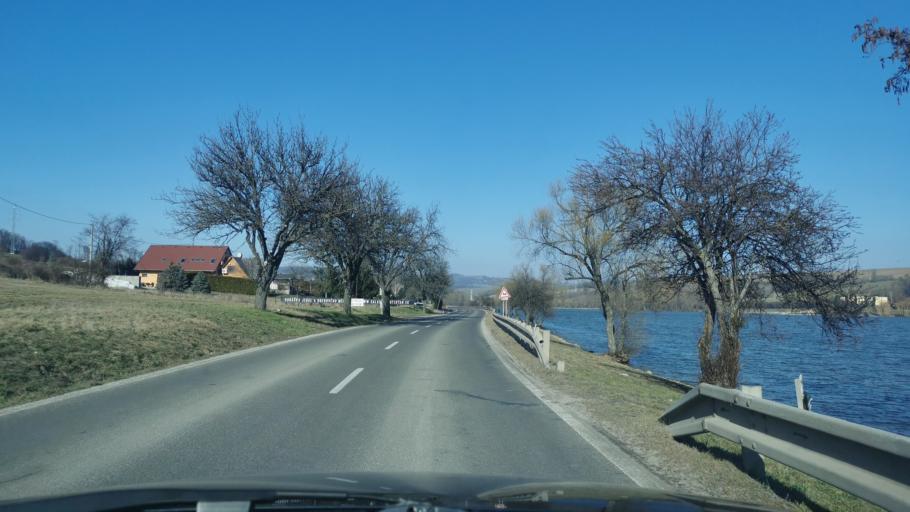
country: SK
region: Trnavsky
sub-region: Okres Senica
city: Senica
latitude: 48.7039
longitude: 17.4008
